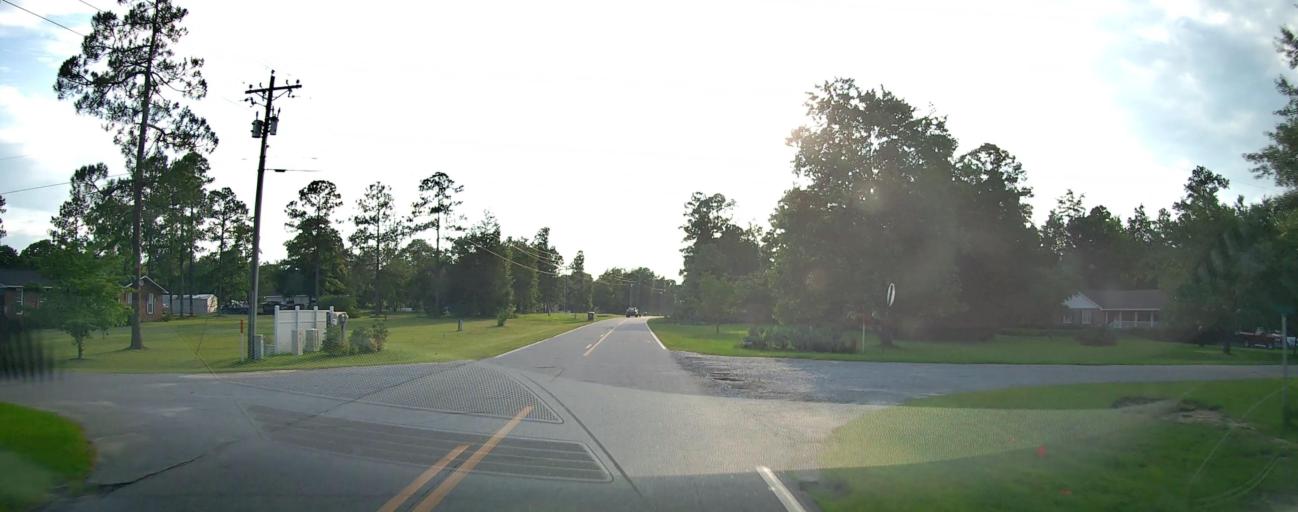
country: US
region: Georgia
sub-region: Peach County
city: Byron
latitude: 32.7044
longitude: -83.8229
